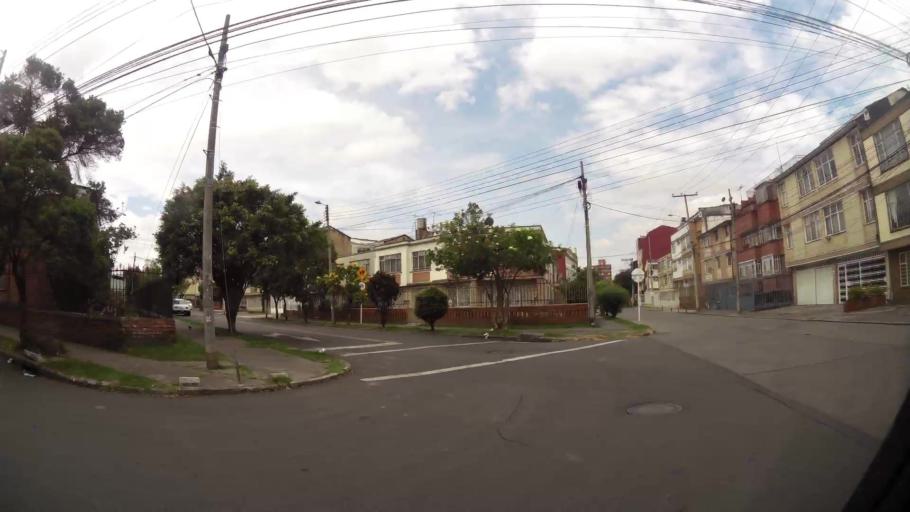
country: CO
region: Bogota D.C.
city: Bogota
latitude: 4.6326
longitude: -74.0768
